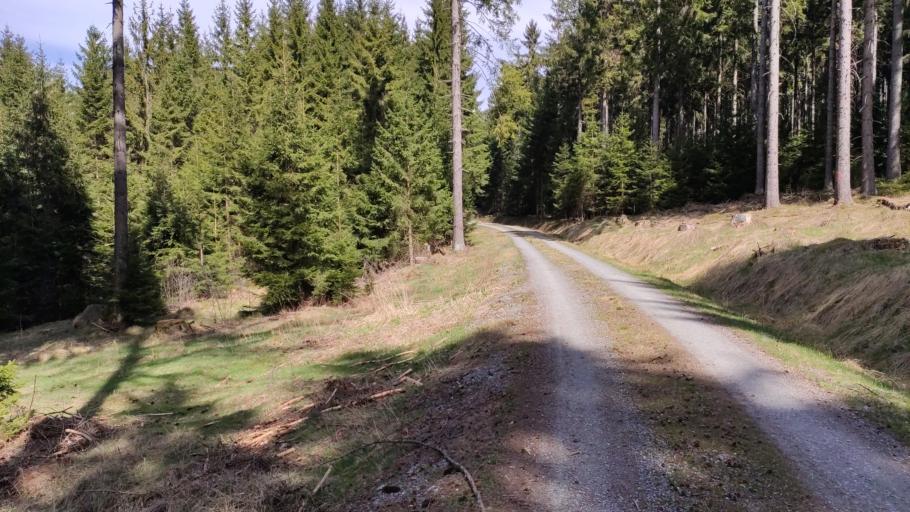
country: DE
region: Bavaria
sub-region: Upper Franconia
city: Reichenbach
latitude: 50.4462
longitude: 11.4408
